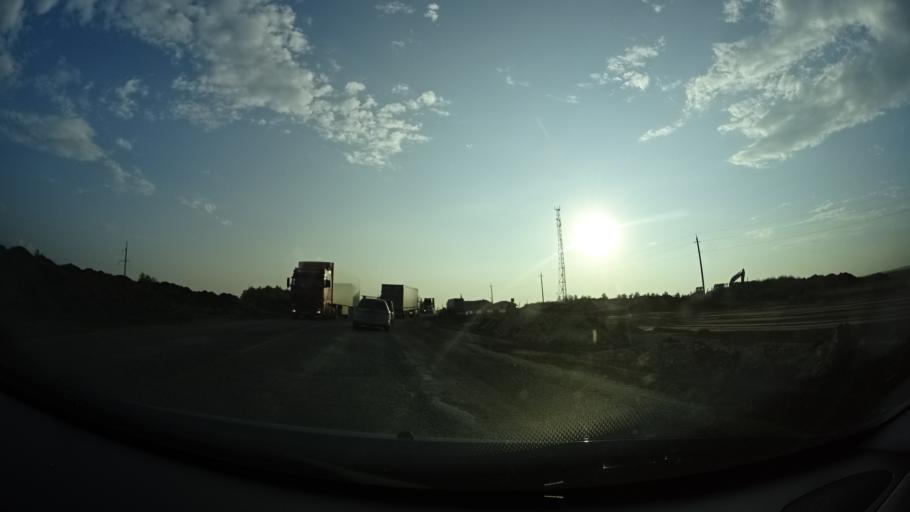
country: RU
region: Samara
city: Kamyshla
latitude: 54.0448
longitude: 52.0014
